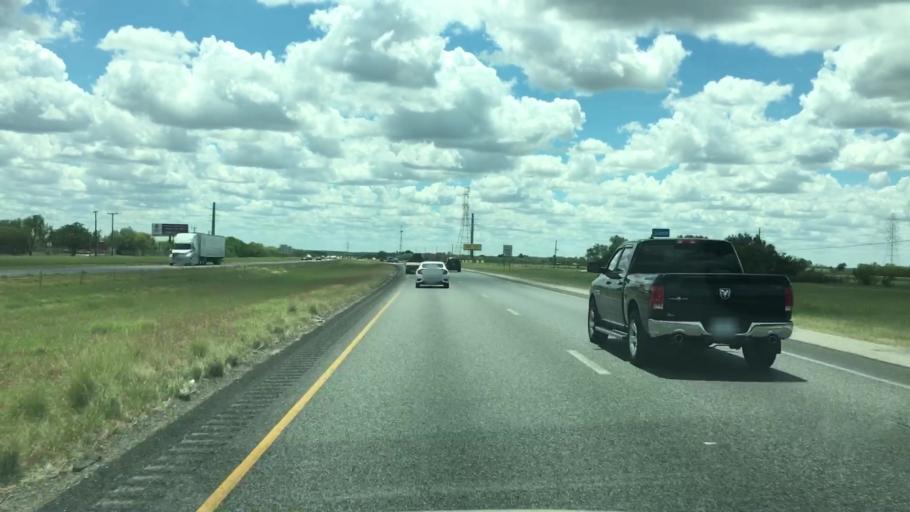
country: US
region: Texas
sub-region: Bexar County
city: Elmendorf
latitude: 29.2737
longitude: -98.3963
